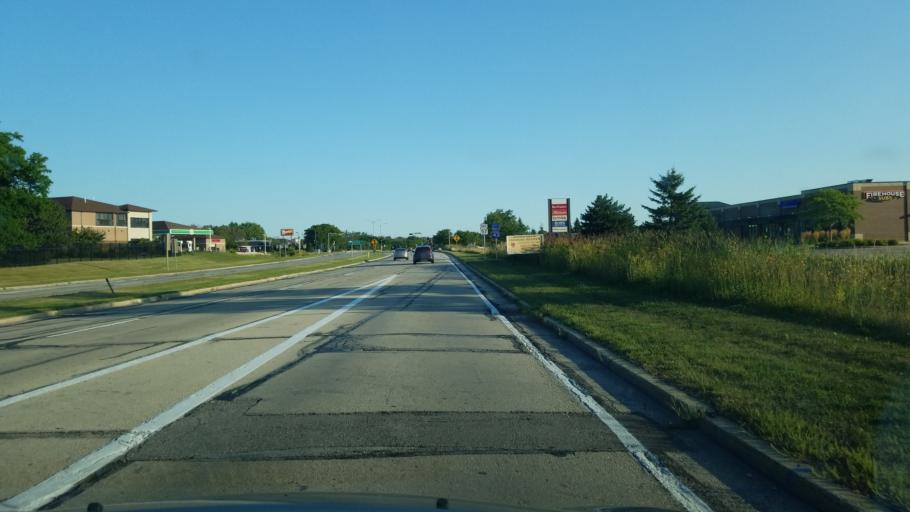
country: US
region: Wisconsin
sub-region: Milwaukee County
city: Brown Deer
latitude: 43.1808
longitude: -87.9622
